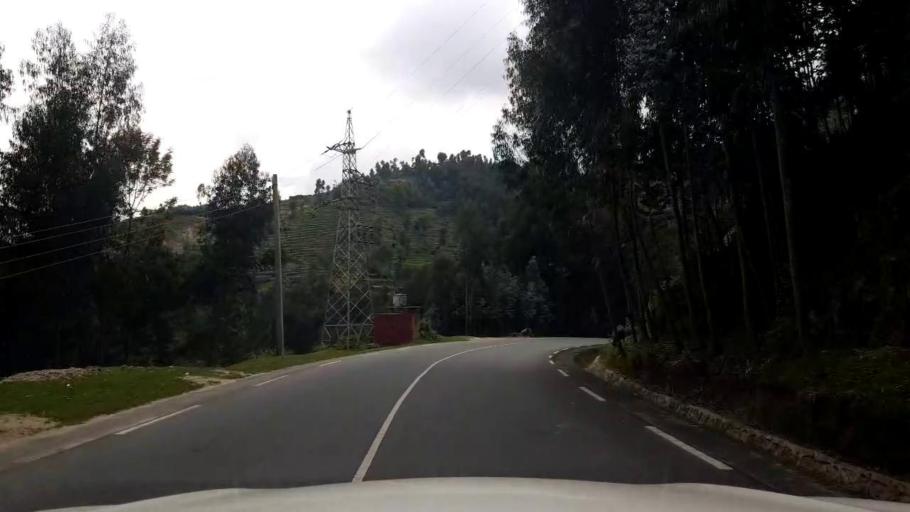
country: RW
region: Northern Province
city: Musanze
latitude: -1.6675
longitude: 29.5149
